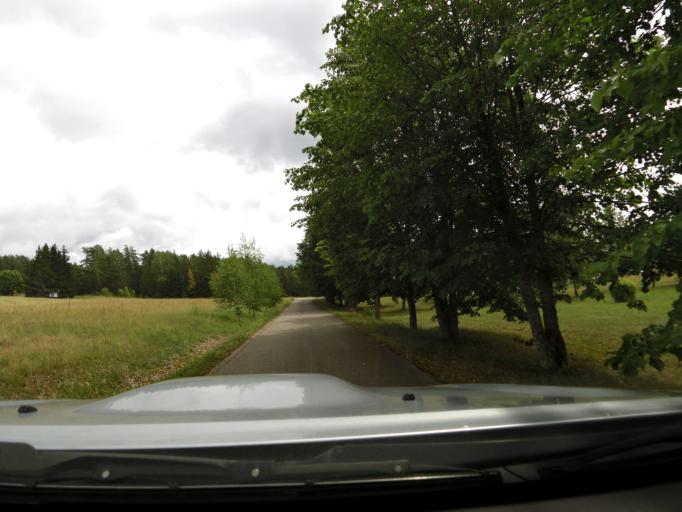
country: LT
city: Moletai
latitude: 55.3166
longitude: 25.5571
